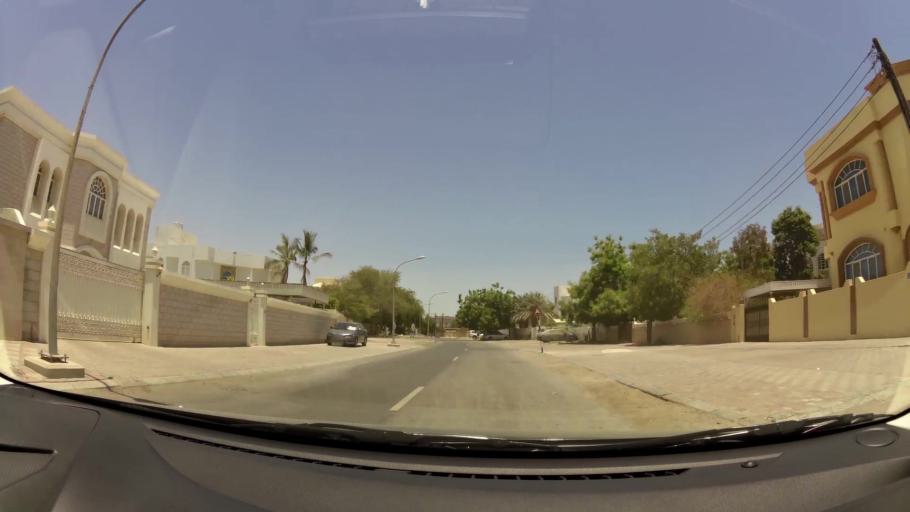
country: OM
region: Muhafazat Masqat
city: As Sib al Jadidah
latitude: 23.6353
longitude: 58.2380
